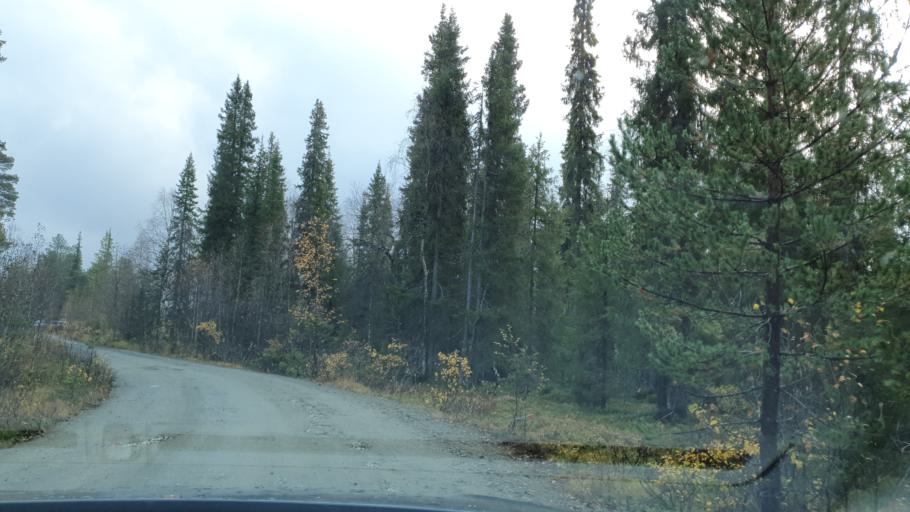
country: FI
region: Lapland
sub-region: Tunturi-Lappi
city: Kolari
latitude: 67.6047
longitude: 24.2127
